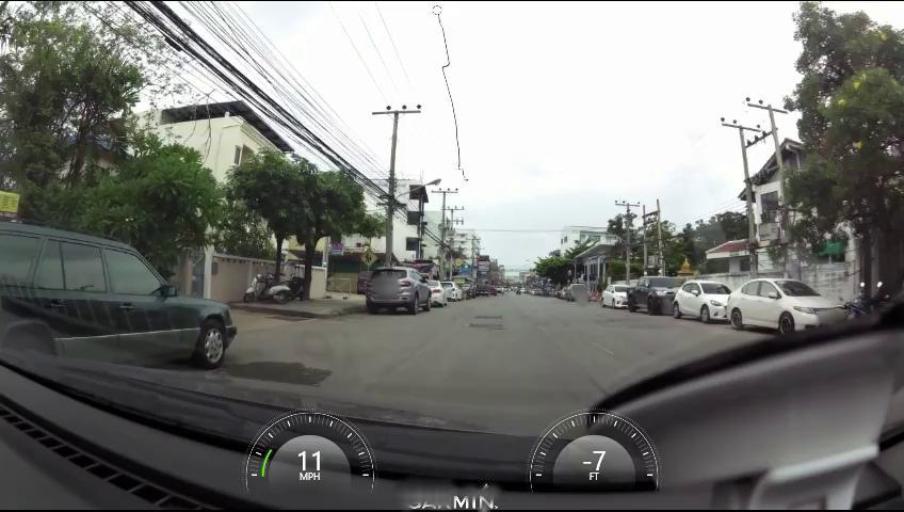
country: TH
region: Prachuap Khiri Khan
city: Hua Hin
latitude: 12.5765
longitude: 99.9564
